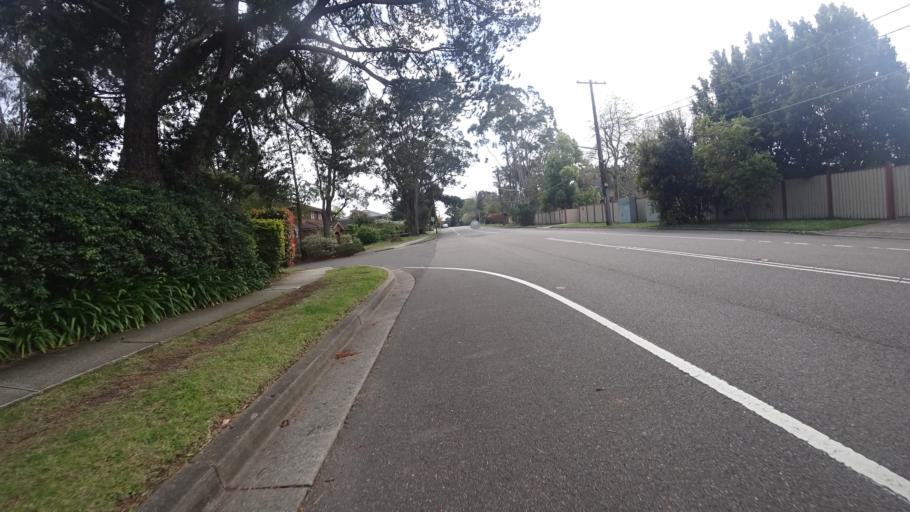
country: AU
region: New South Wales
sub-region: City of Sydney
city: North Turramurra
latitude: -33.6945
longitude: 151.1515
